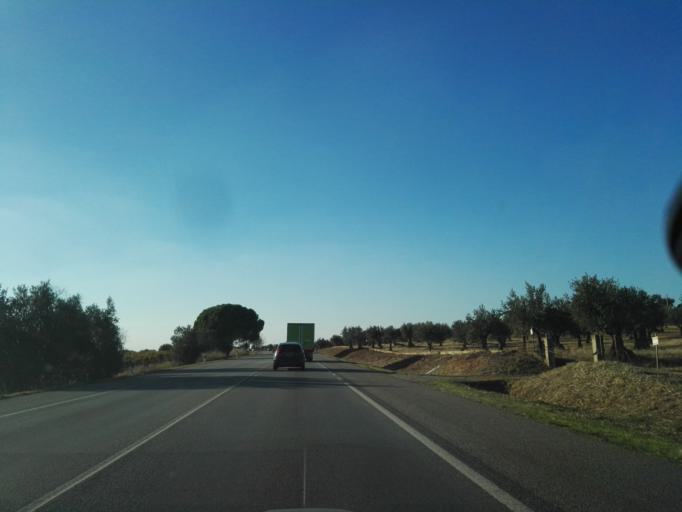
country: PT
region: Evora
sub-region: Estremoz
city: Estremoz
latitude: 38.8299
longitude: -7.5331
